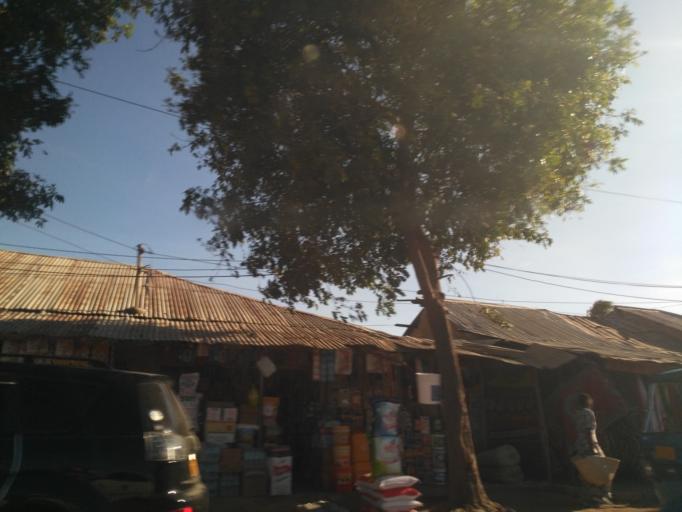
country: TZ
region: Dodoma
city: Dodoma
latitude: -6.1784
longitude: 35.7410
